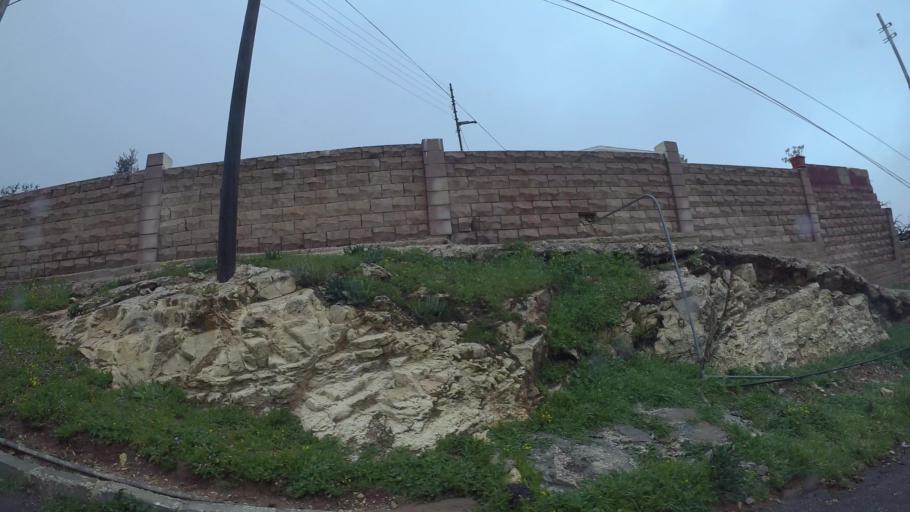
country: JO
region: Amman
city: Wadi as Sir
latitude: 32.0035
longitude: 35.7980
